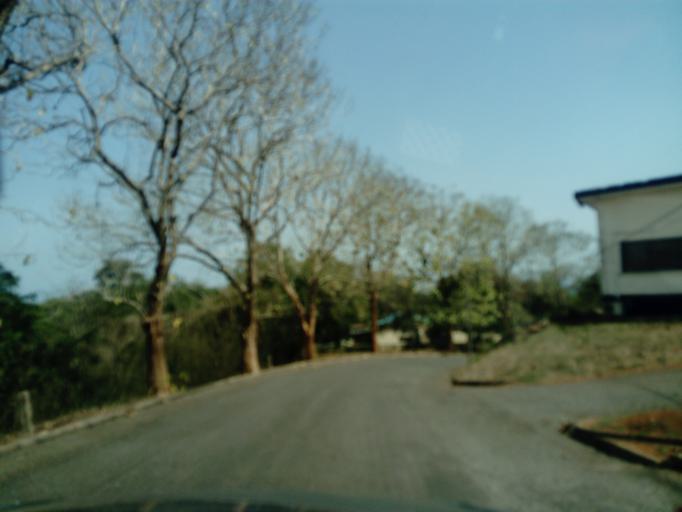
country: GH
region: Central
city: Cape Coast
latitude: 5.1076
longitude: -1.2827
